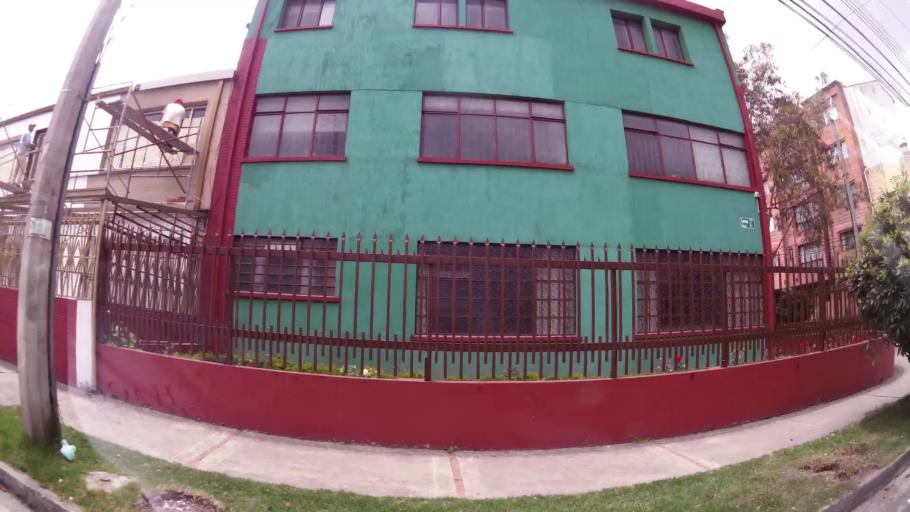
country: CO
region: Bogota D.C.
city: Bogota
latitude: 4.6320
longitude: -74.0784
